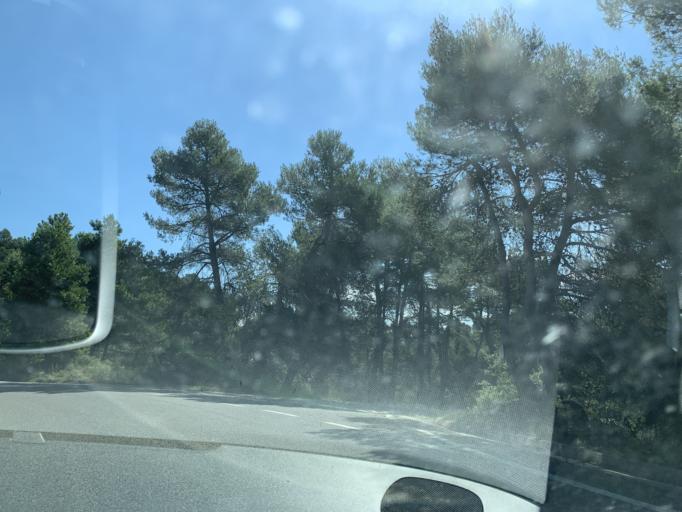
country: ES
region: Catalonia
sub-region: Provincia de Tarragona
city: Conesa
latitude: 41.5402
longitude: 1.3089
